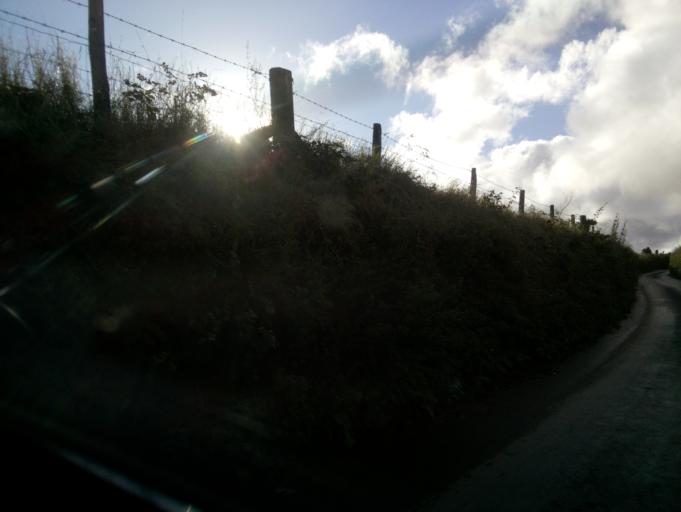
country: GB
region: England
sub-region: Devon
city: Totnes
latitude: 50.3640
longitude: -3.7382
